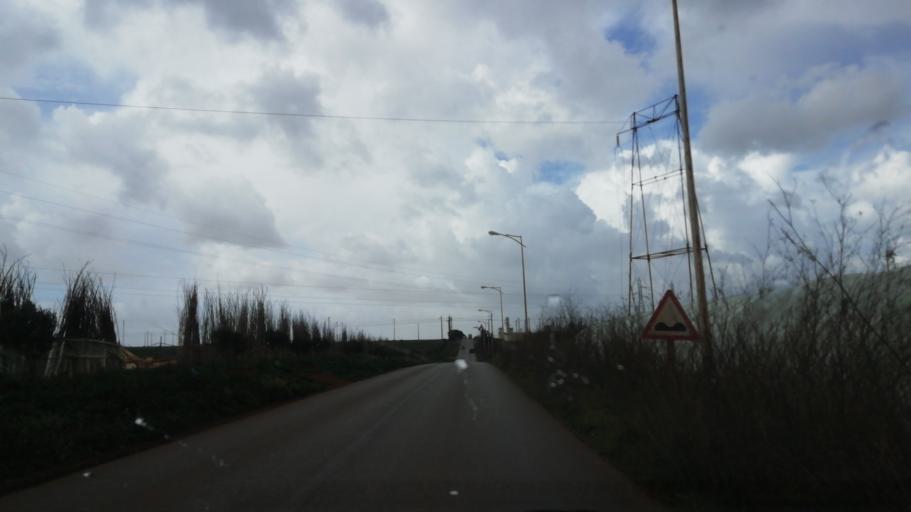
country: DZ
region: Oran
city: Sidi ech Chahmi
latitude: 35.6275
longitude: -0.5296
